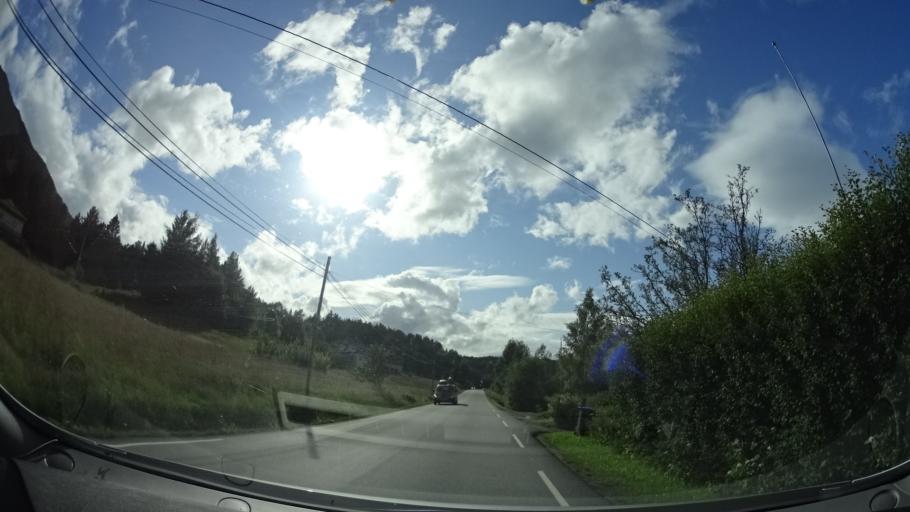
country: NO
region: More og Romsdal
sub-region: Halsa
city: Liaboen
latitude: 63.1355
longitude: 8.4426
